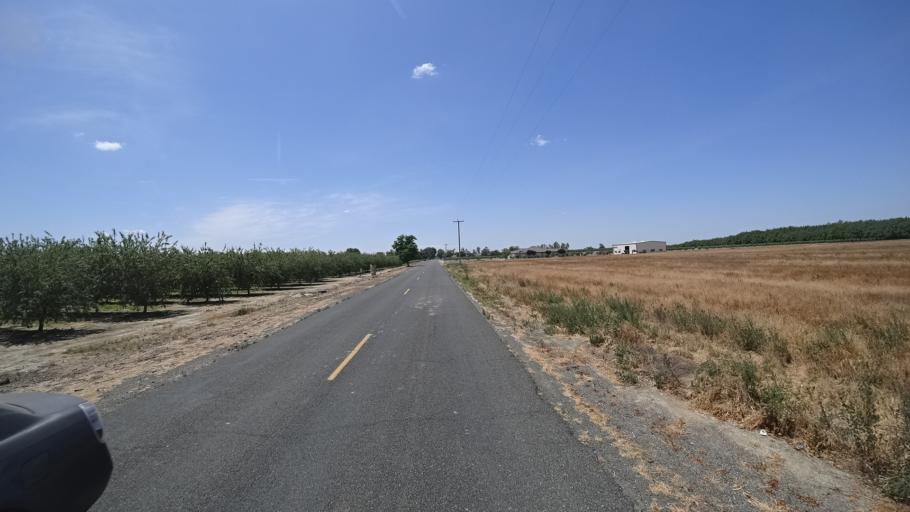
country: US
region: California
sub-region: Kings County
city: Armona
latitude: 36.2839
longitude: -119.7313
